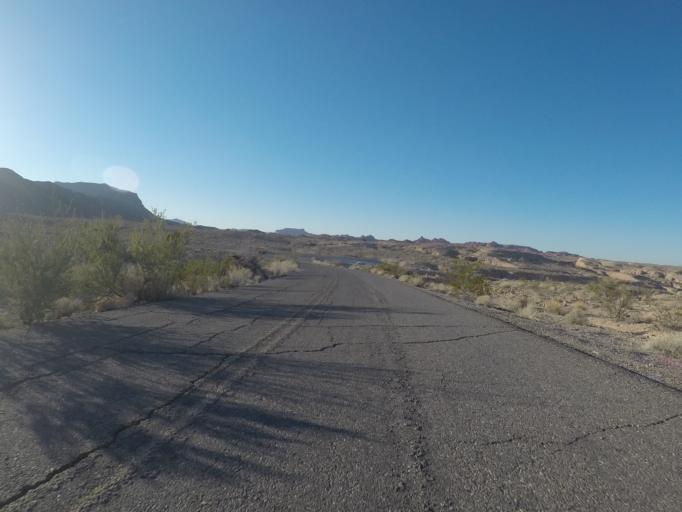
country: US
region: Nevada
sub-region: Clark County
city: Moapa Valley
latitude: 36.3941
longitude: -114.4239
